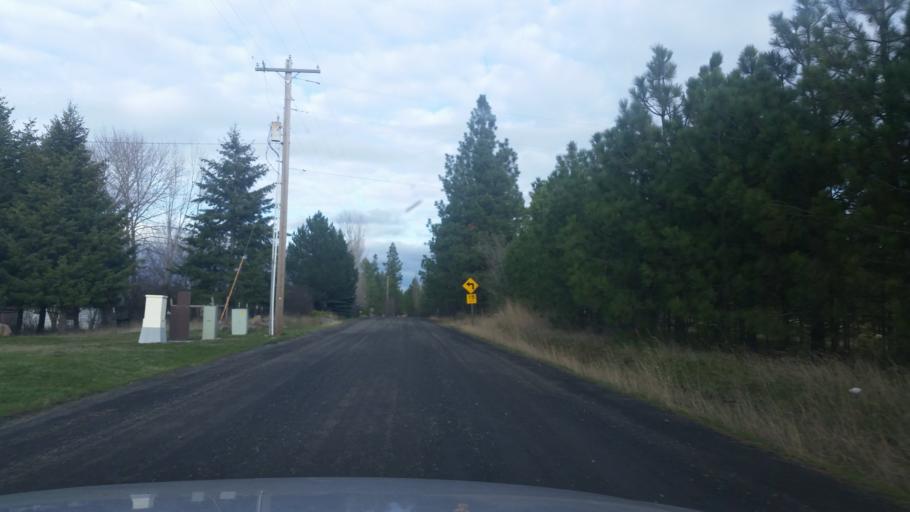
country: US
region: Washington
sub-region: Spokane County
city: Cheney
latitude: 47.4249
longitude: -117.4661
